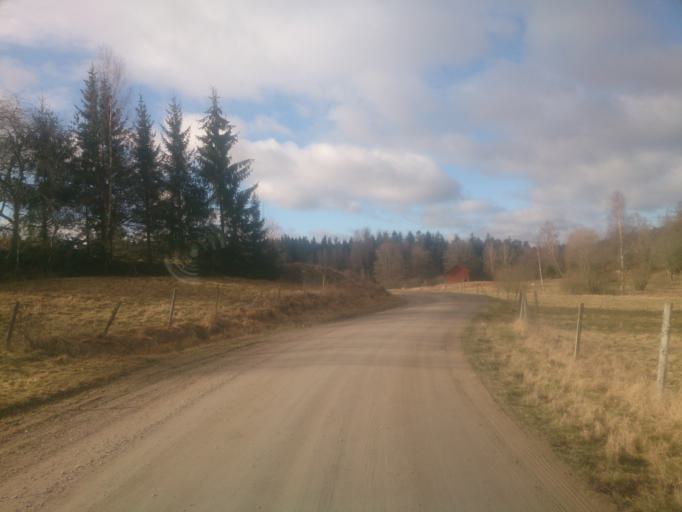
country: SE
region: OEstergoetland
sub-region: Atvidabergs Kommun
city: Atvidaberg
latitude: 58.2202
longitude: 16.1677
